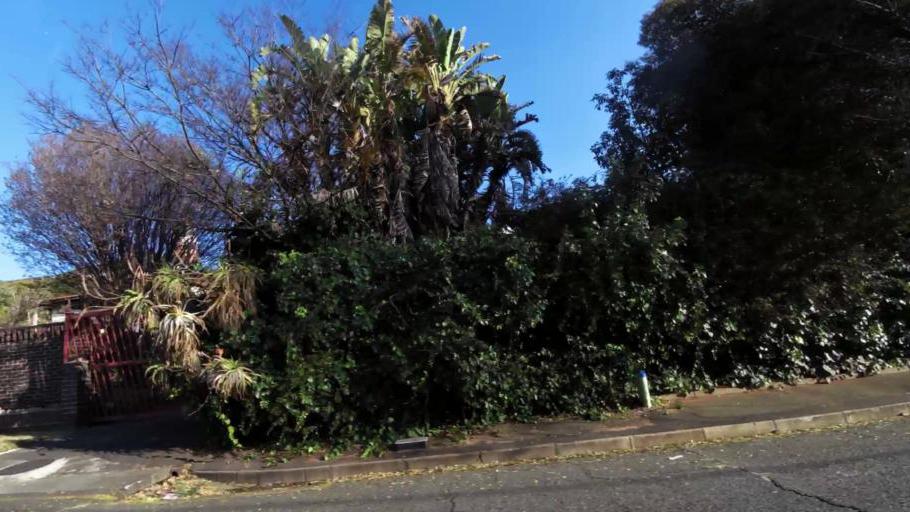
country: ZA
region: Gauteng
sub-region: City of Johannesburg Metropolitan Municipality
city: Johannesburg
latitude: -26.1899
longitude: 28.0002
